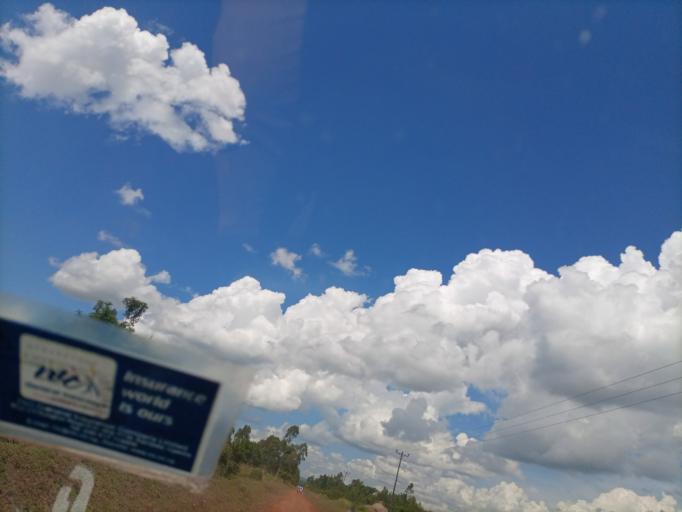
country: UG
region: Eastern Region
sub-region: Tororo District
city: Tororo
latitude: 0.6636
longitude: 34.0015
